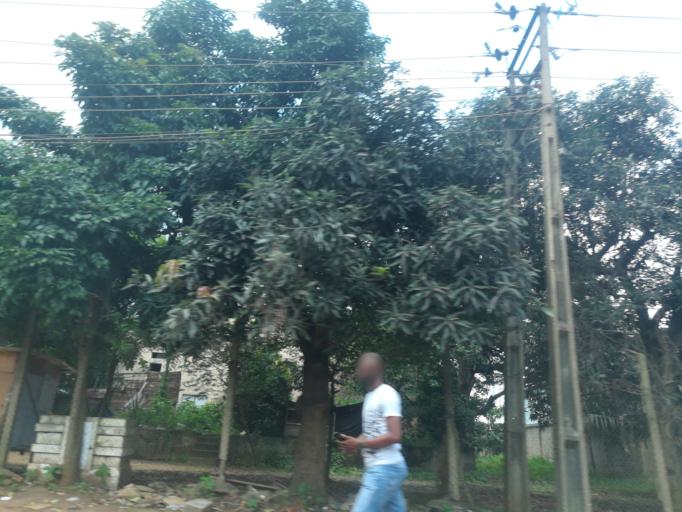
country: NG
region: Lagos
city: Ikeja
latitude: 6.6066
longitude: 3.3644
